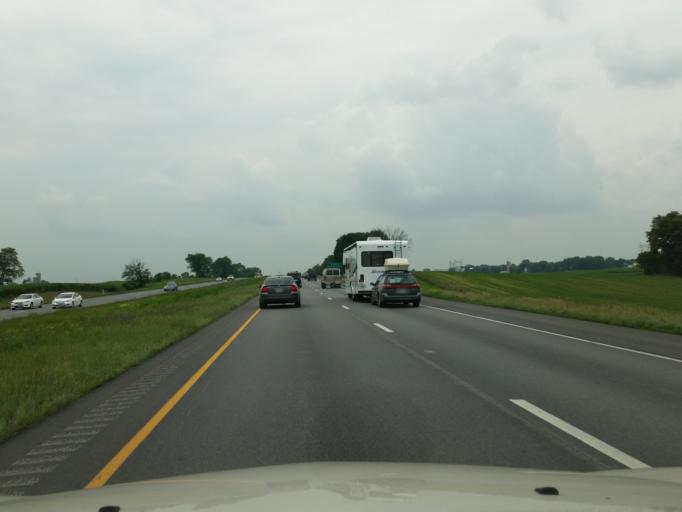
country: US
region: Pennsylvania
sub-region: Lancaster County
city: Mount Joy
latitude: 40.1285
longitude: -76.5194
